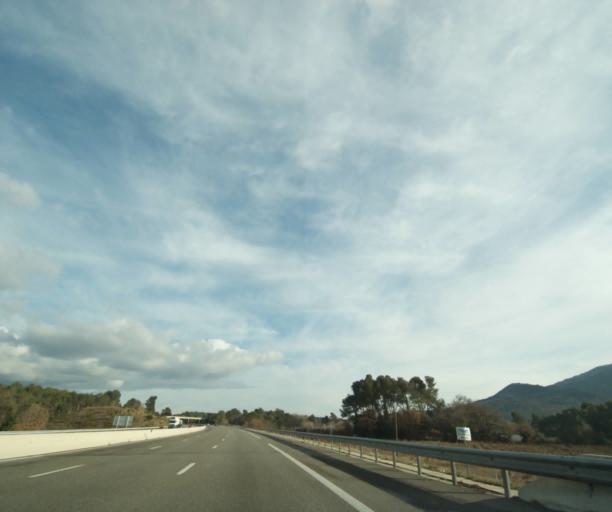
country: FR
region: Provence-Alpes-Cote d'Azur
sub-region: Departement du Var
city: Pourrieres
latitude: 43.4790
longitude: 5.7506
